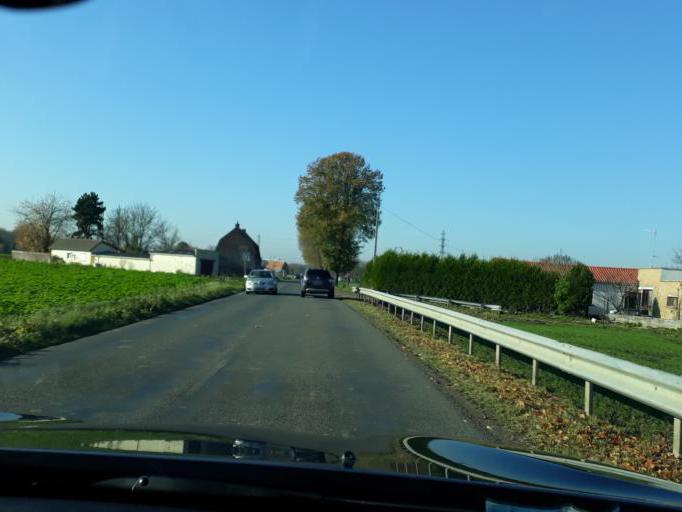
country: FR
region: Nord-Pas-de-Calais
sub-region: Departement du Nord
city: Guesnain
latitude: 50.3624
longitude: 3.1463
